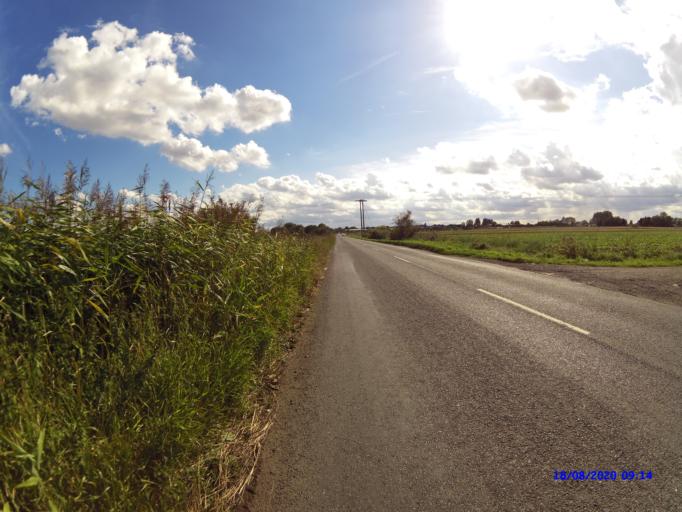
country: GB
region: England
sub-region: Cambridgeshire
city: Ramsey
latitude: 52.4617
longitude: -0.1028
